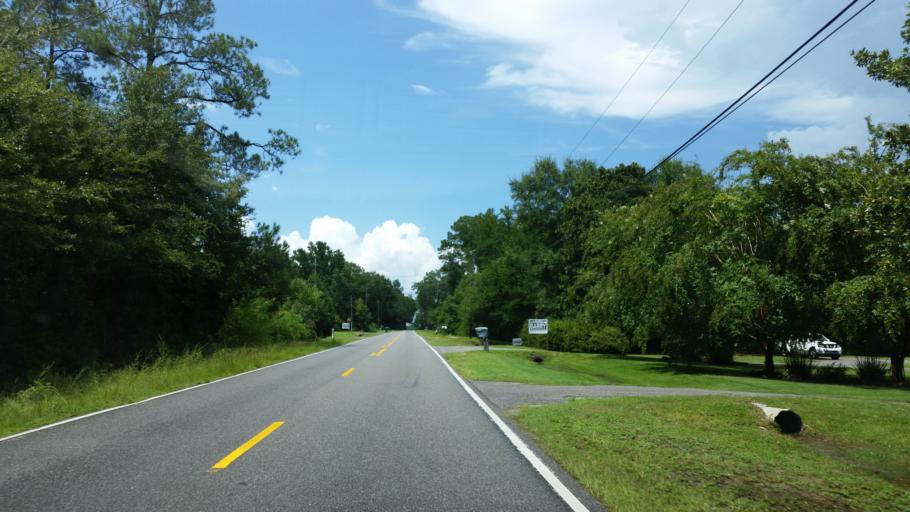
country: US
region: Florida
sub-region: Escambia County
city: Gonzalez
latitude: 30.5535
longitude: -87.2998
